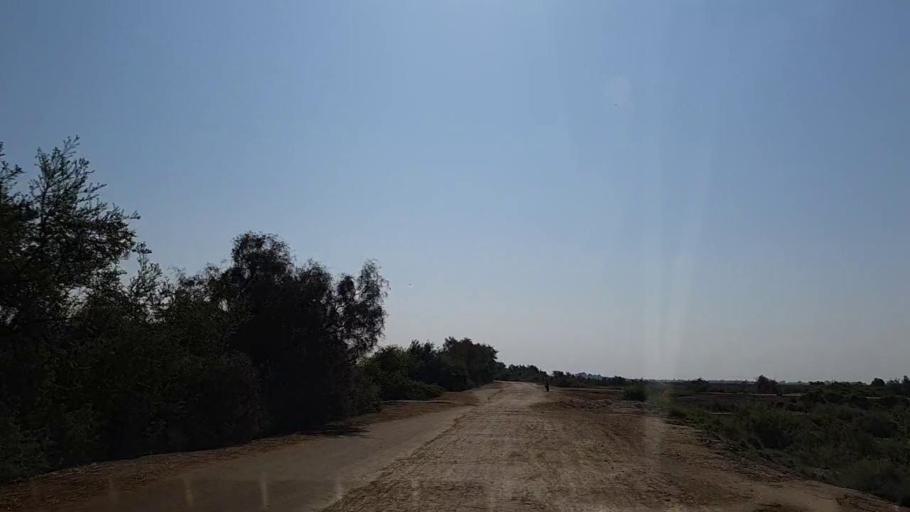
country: PK
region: Sindh
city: Chuhar Jamali
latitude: 24.5151
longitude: 68.0956
